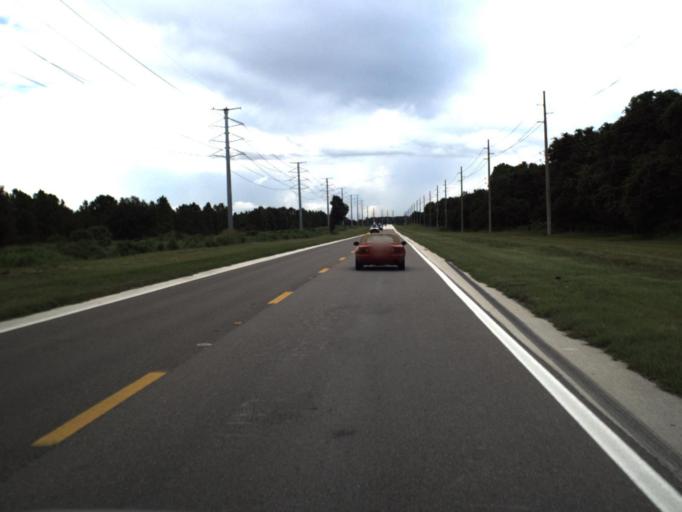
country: US
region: Florida
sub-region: Polk County
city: Mulberry
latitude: 27.7571
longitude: -81.9939
